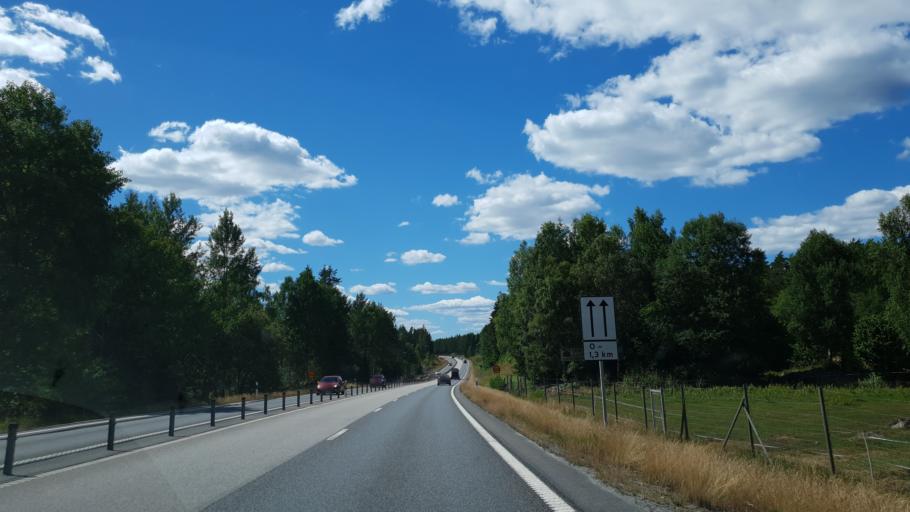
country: SE
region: Kronoberg
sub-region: Vaxjo Kommun
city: Ingelstad
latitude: 56.8698
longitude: 14.9690
